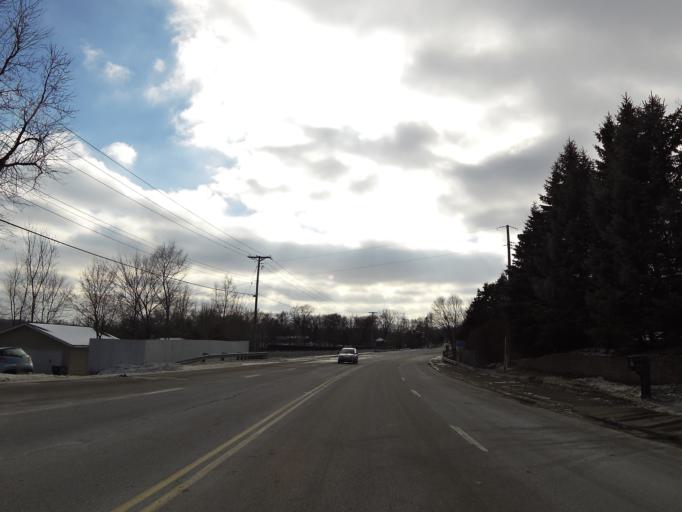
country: US
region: Minnesota
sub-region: Hennepin County
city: Hopkins
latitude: 44.8927
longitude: -93.4693
